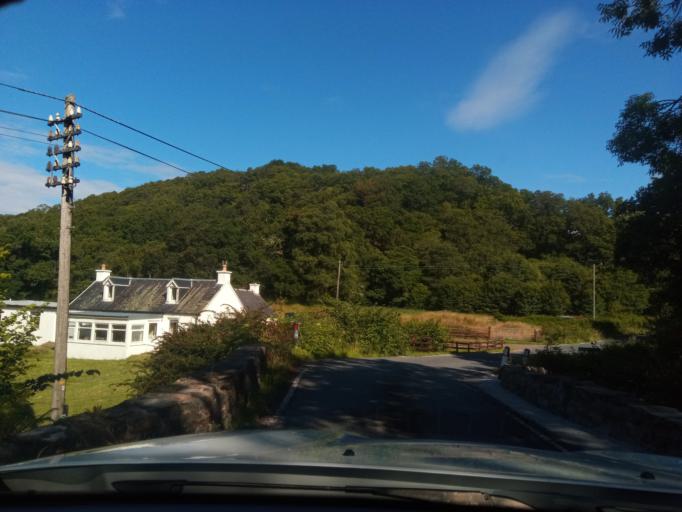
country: GB
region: Scotland
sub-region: Argyll and Bute
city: Isle Of Mull
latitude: 56.6899
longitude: -5.6684
